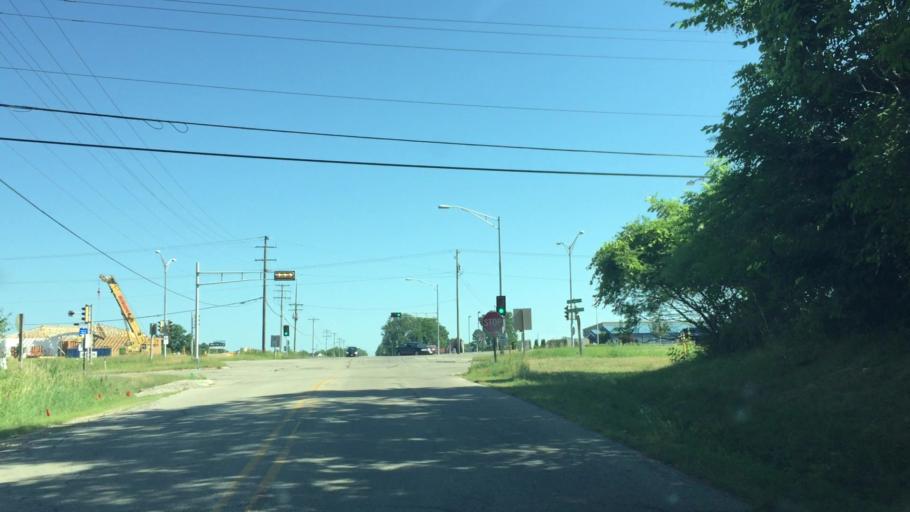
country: US
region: Wisconsin
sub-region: Outagamie County
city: Kimberly
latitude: 44.2069
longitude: -88.3635
